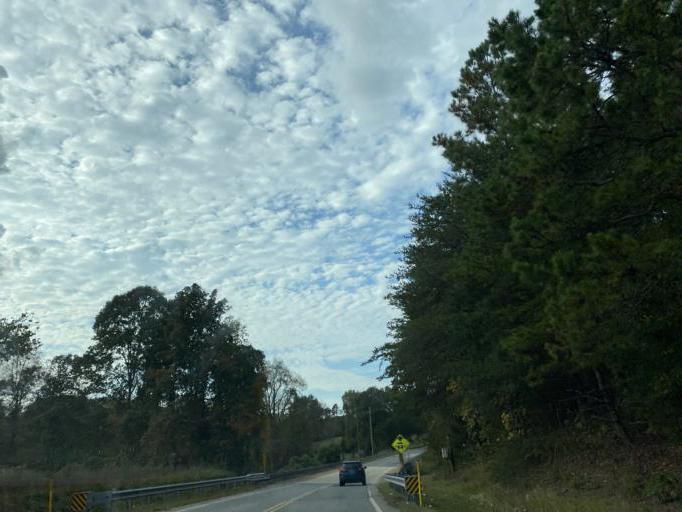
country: US
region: South Carolina
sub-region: Cherokee County
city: Gaffney
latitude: 35.0718
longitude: -81.7230
